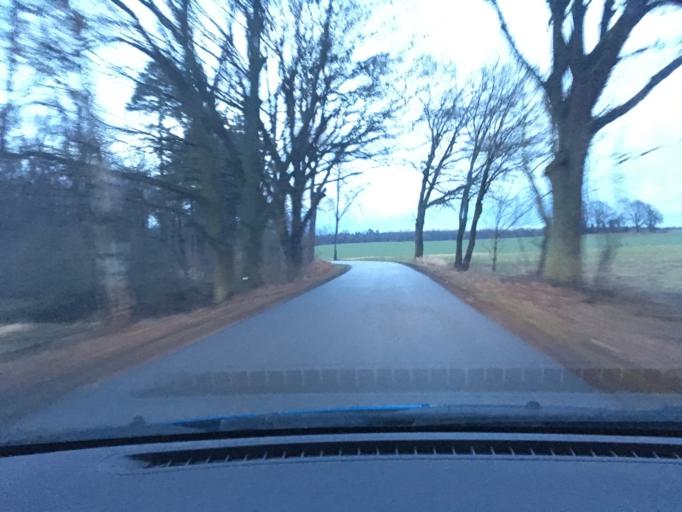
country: DE
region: Lower Saxony
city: Betzendorf
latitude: 53.1516
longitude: 10.3391
